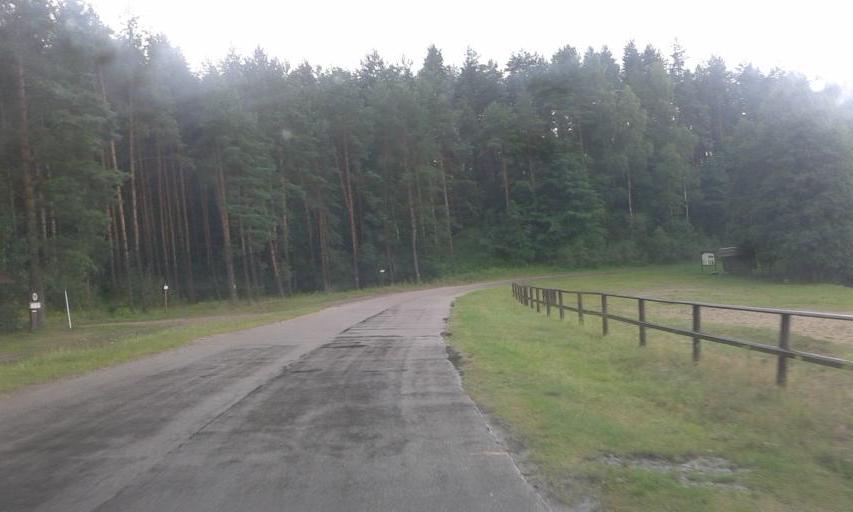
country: PL
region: West Pomeranian Voivodeship
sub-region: Powiat szczecinecki
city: Lubowo
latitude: 53.6179
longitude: 16.3743
